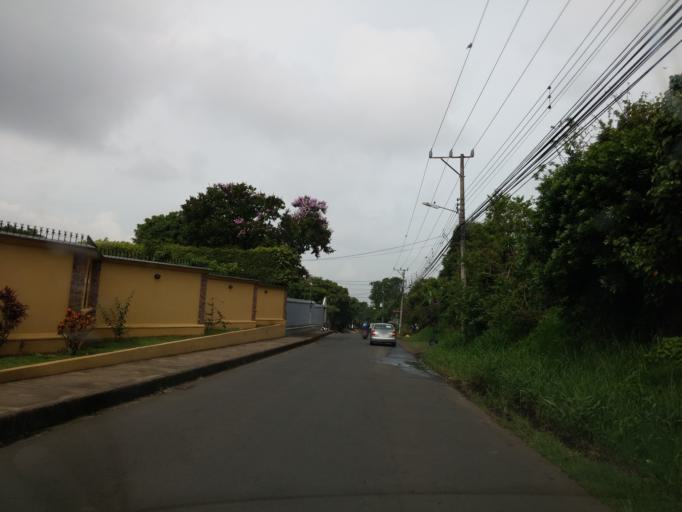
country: CR
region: Heredia
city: Llorente
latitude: 10.0174
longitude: -84.1656
